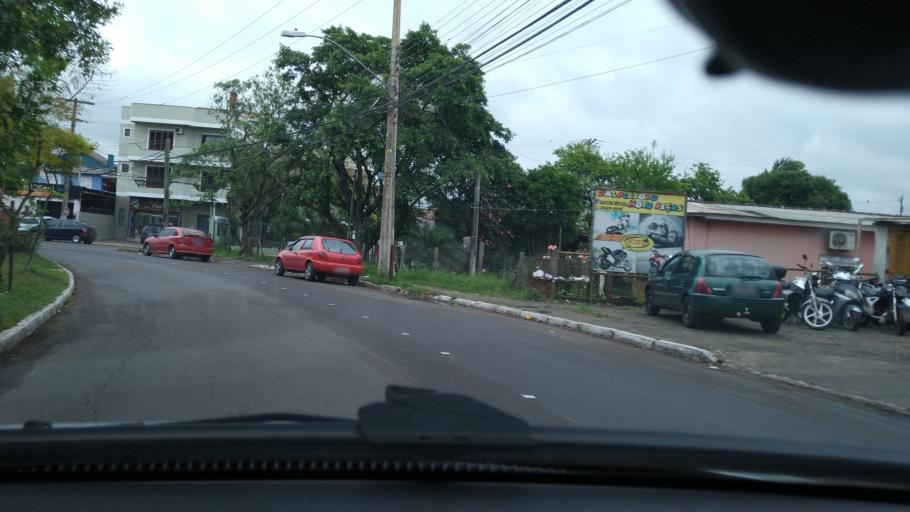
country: BR
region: Rio Grande do Sul
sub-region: Canoas
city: Canoas
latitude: -29.9013
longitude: -51.2051
